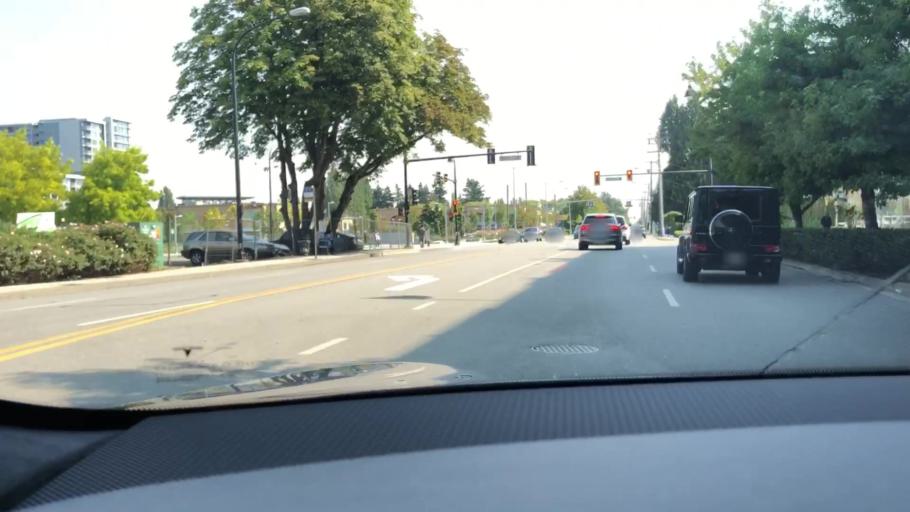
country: CA
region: British Columbia
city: Richmond
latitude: 49.1848
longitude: -123.1337
